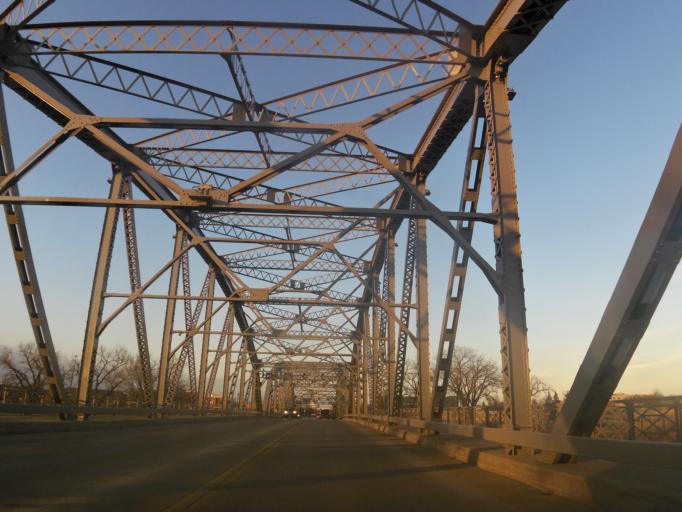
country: US
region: North Dakota
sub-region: Grand Forks County
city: Grand Forks
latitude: 47.9264
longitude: -97.0291
